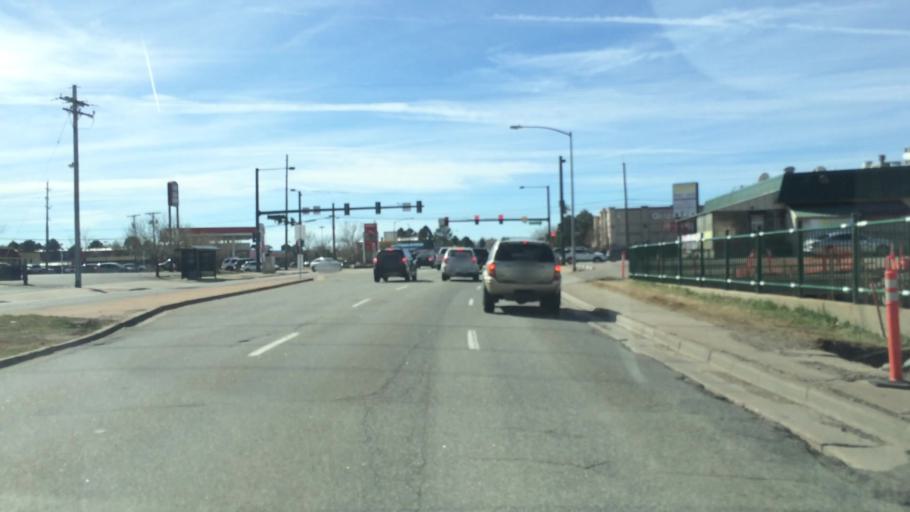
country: US
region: Colorado
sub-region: Arapahoe County
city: Glendale
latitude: 39.6794
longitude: -104.9130
